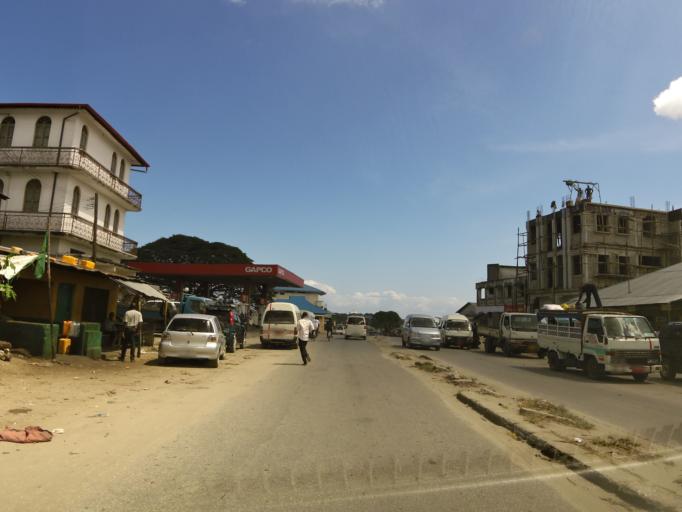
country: TZ
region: Zanzibar Urban/West
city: Zanzibar
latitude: -6.1633
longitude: 39.2117
